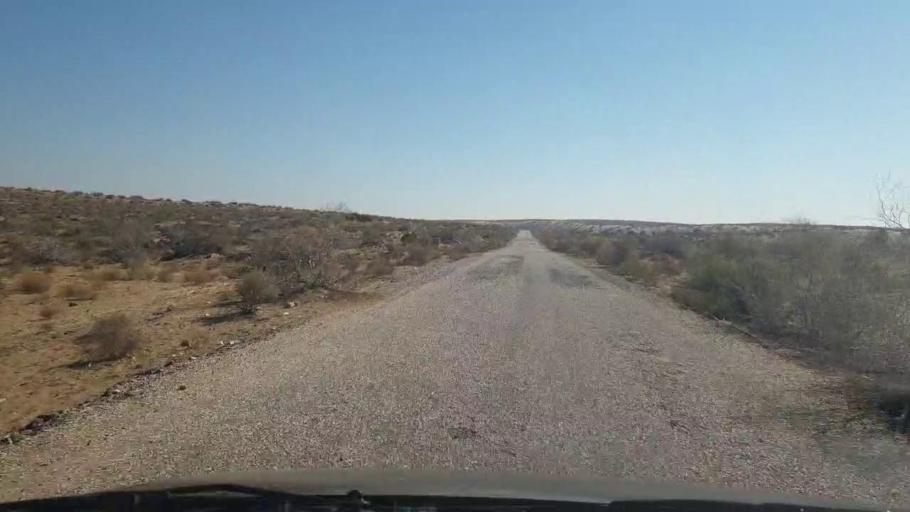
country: PK
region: Sindh
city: Bozdar
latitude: 27.0260
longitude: 68.7111
